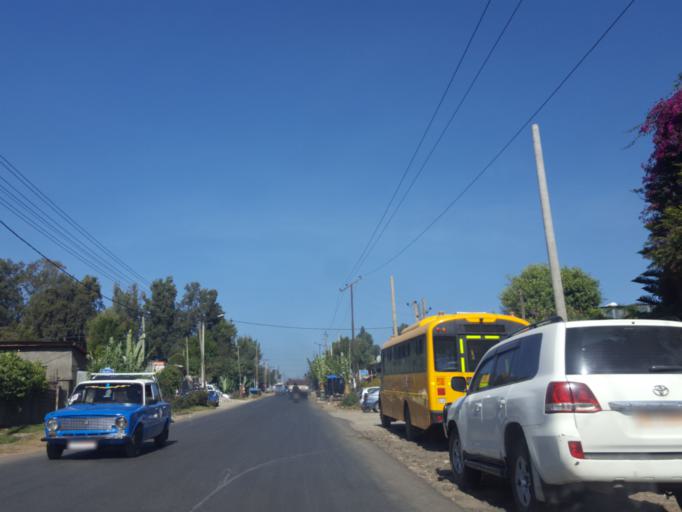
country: ET
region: Adis Abeba
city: Addis Ababa
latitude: 9.0516
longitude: 38.7367
